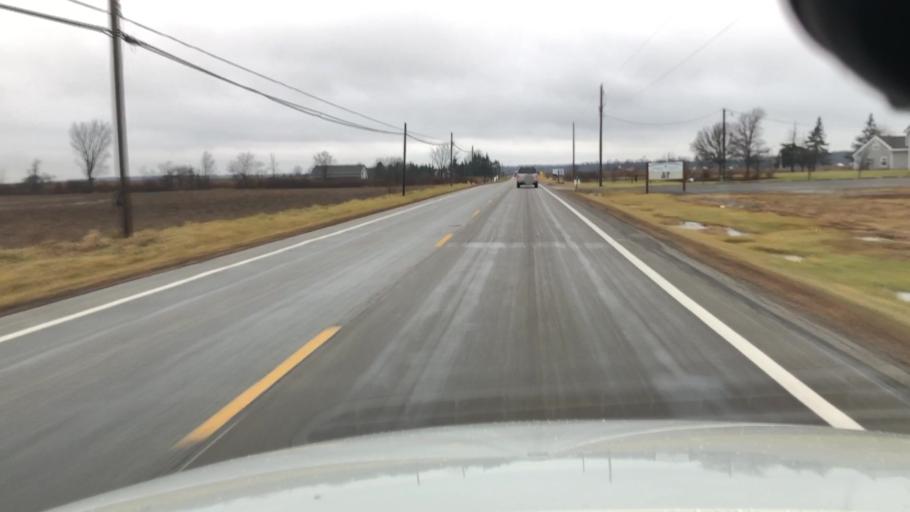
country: US
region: Ohio
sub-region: Allen County
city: Lima
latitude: 40.7069
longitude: -84.0045
